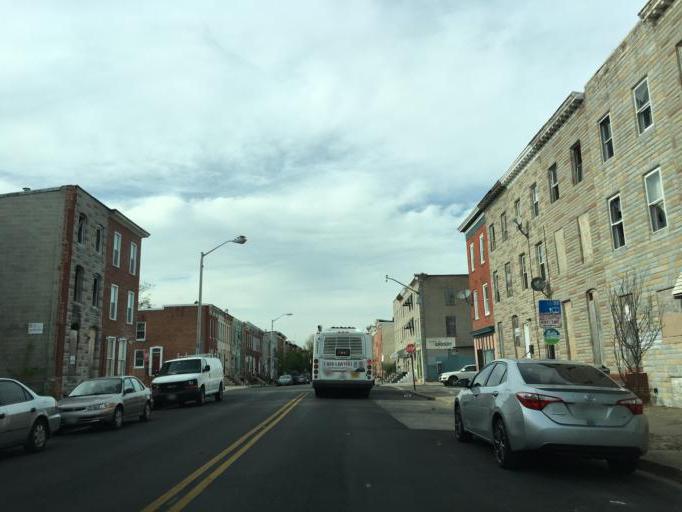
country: US
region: Maryland
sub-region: City of Baltimore
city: Baltimore
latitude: 39.2839
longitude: -76.6421
